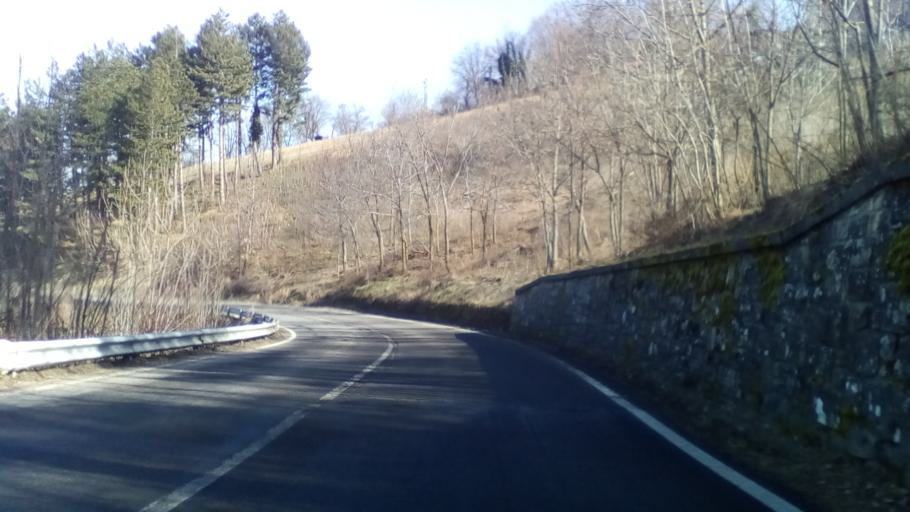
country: IT
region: Emilia-Romagna
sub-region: Provincia di Modena
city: Lama
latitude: 44.3006
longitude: 10.7166
